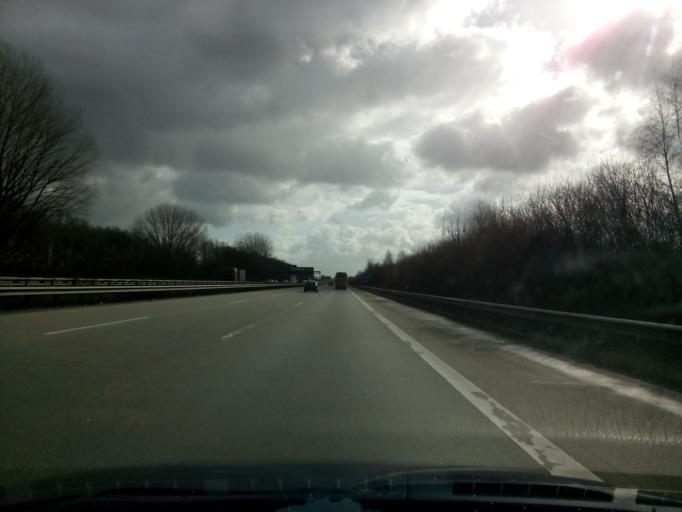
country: DE
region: Lower Saxony
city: Ritterhude
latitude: 53.1365
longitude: 8.7482
